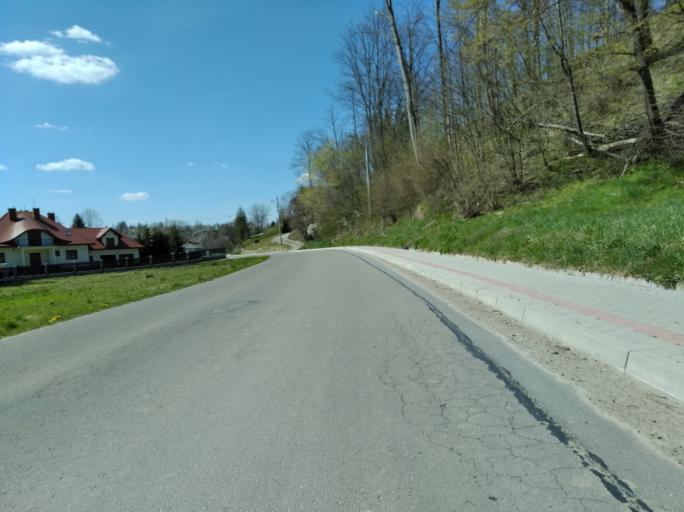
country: PL
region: Subcarpathian Voivodeship
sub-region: Powiat brzozowski
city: Golcowa
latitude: 49.7700
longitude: 22.0316
